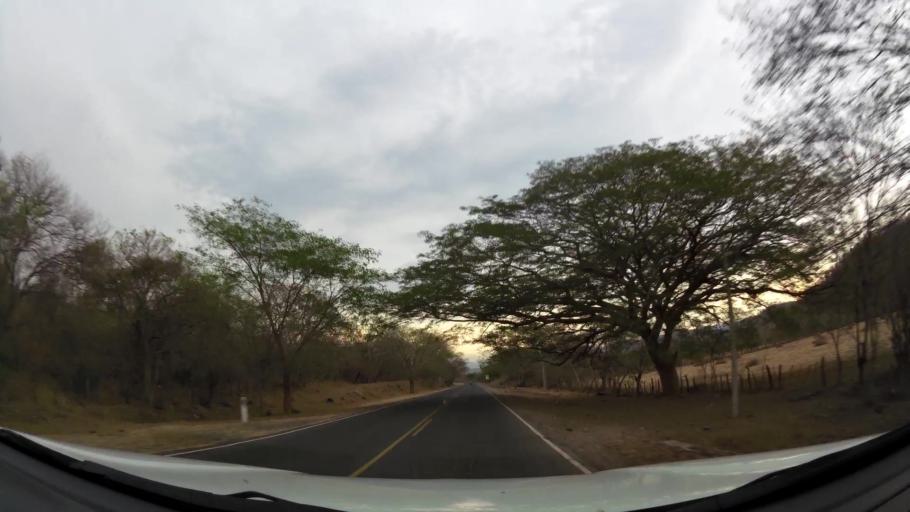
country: NI
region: Leon
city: La Jicaral
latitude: 12.7057
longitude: -86.3969
